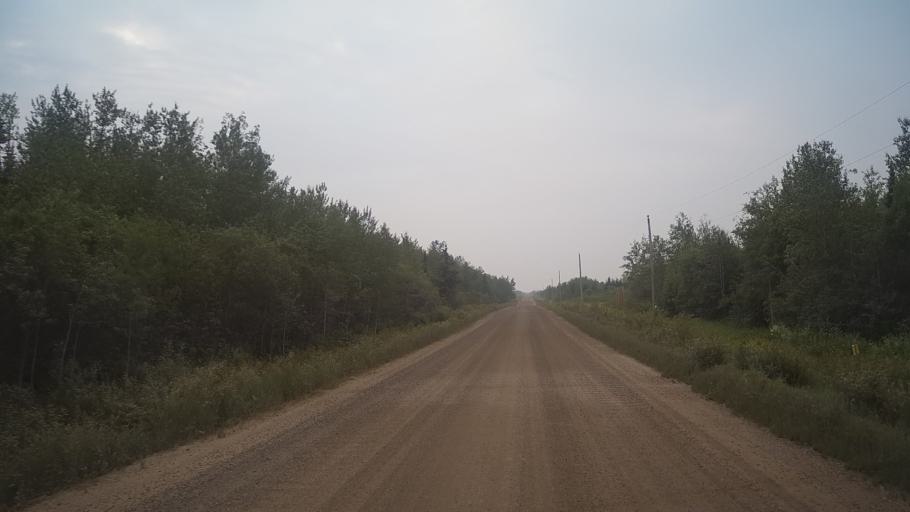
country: CA
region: Ontario
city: Hearst
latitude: 49.6384
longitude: -83.2783
